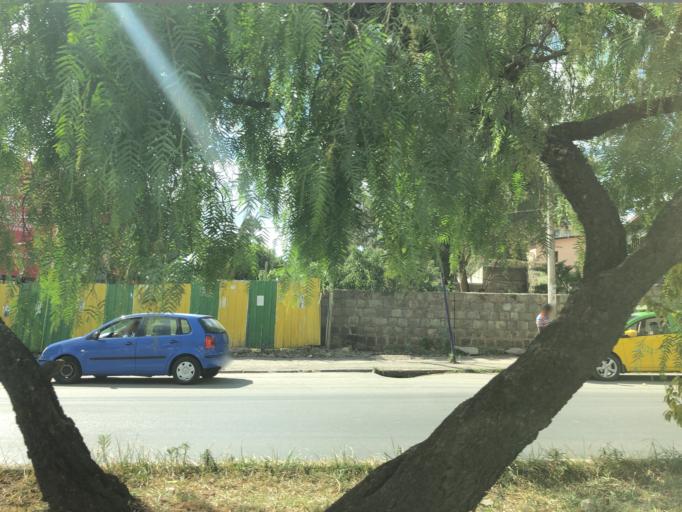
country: ET
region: Adis Abeba
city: Addis Ababa
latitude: 8.9991
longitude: 38.7794
